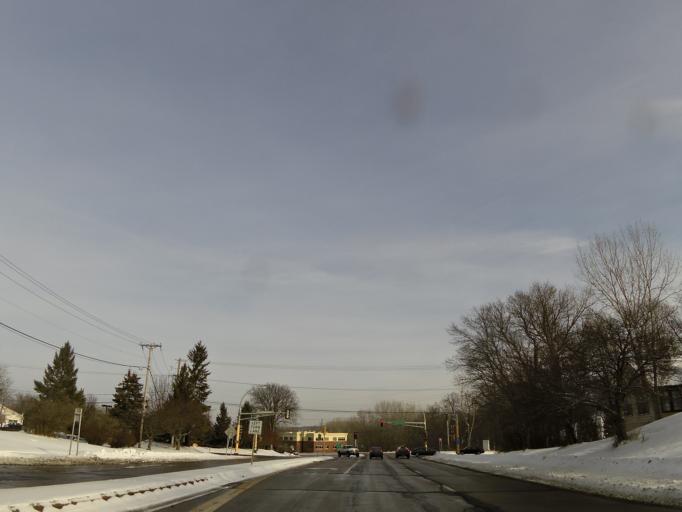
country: US
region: Minnesota
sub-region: Hennepin County
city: Minnetonka
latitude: 44.9081
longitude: -93.5045
